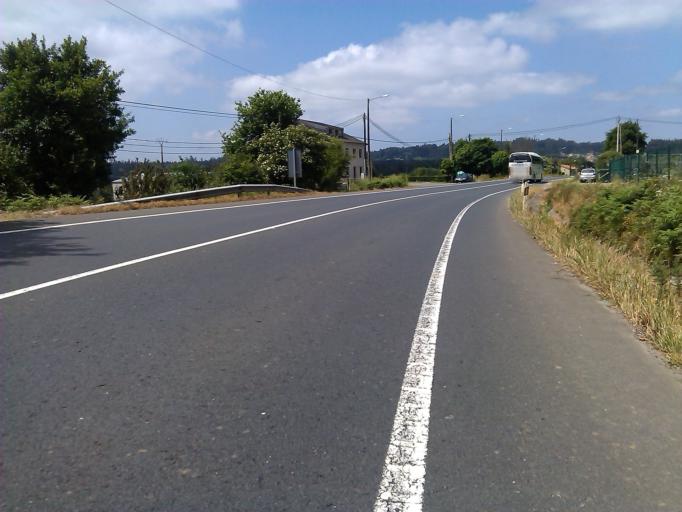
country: ES
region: Galicia
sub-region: Provincia da Coruna
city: Touro
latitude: 42.9184
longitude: -8.3022
